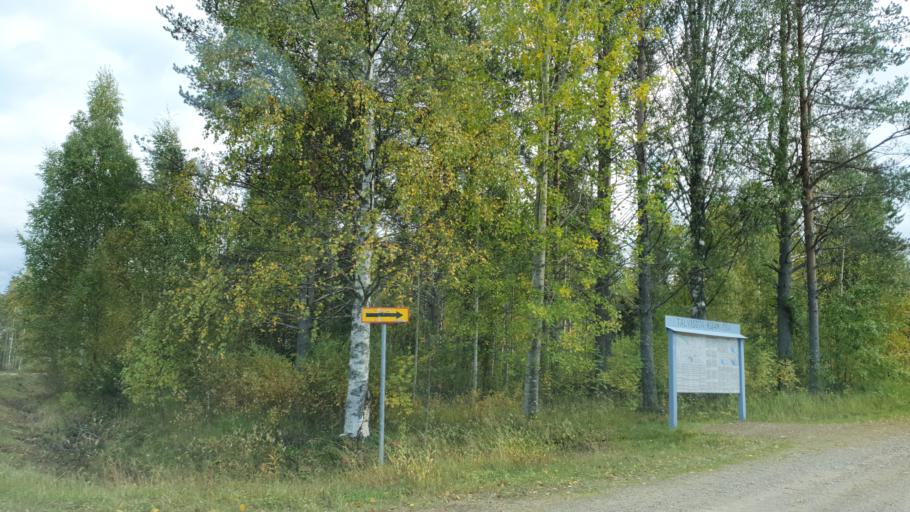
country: FI
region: Kainuu
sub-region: Kehys-Kainuu
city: Kuhmo
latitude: 63.9477
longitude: 29.8817
